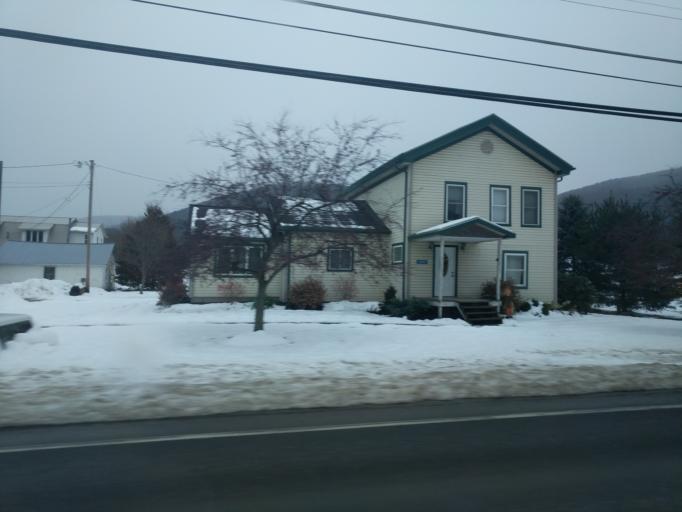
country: US
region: Pennsylvania
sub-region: Tioga County
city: Wellsboro
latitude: 41.8262
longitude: -77.2876
